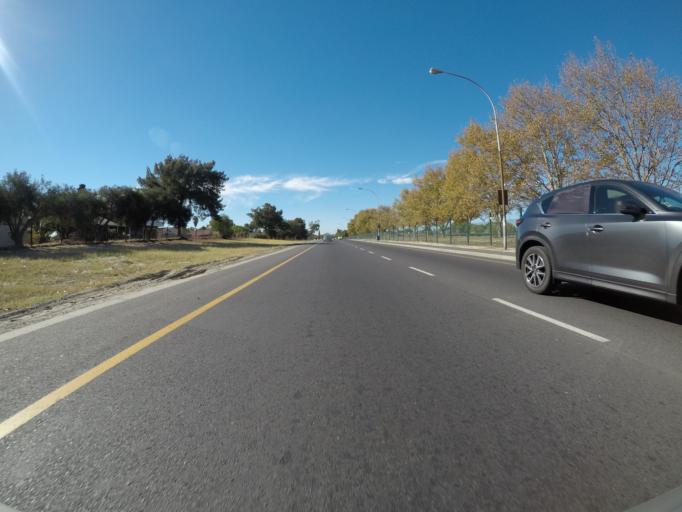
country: ZA
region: Western Cape
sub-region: City of Cape Town
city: Kraaifontein
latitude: -33.9395
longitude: 18.6768
